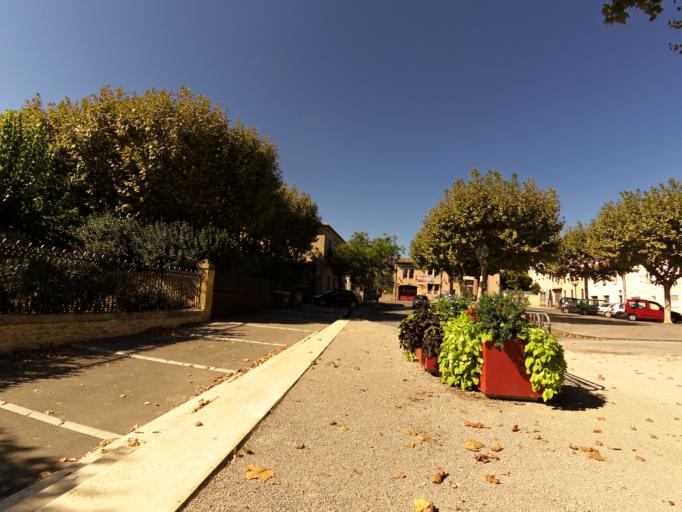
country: FR
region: Languedoc-Roussillon
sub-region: Departement du Gard
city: Vergeze
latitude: 43.7426
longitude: 4.2203
